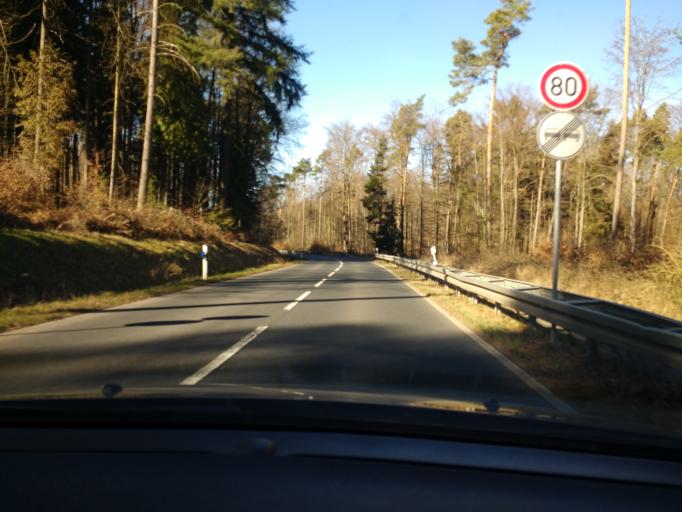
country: DE
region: Bavaria
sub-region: Regierungsbezirk Unterfranken
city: Alzenau in Unterfranken
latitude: 50.1266
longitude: 9.0824
